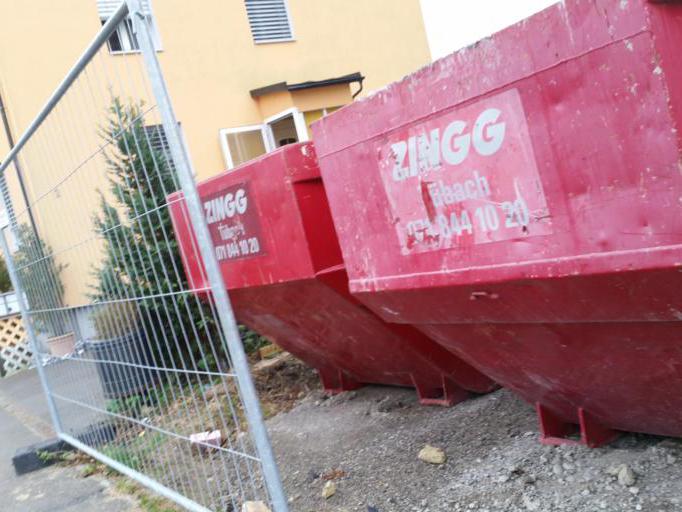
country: CH
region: Thurgau
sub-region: Arbon District
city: Salmsach
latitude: 47.5553
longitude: 9.3712
